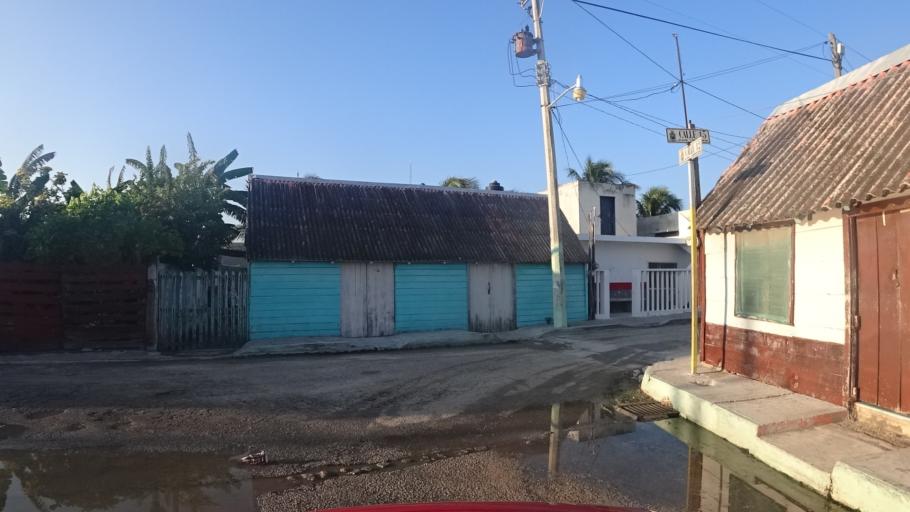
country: MX
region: Yucatan
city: Rio Lagartos
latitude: 21.5972
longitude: -88.1585
